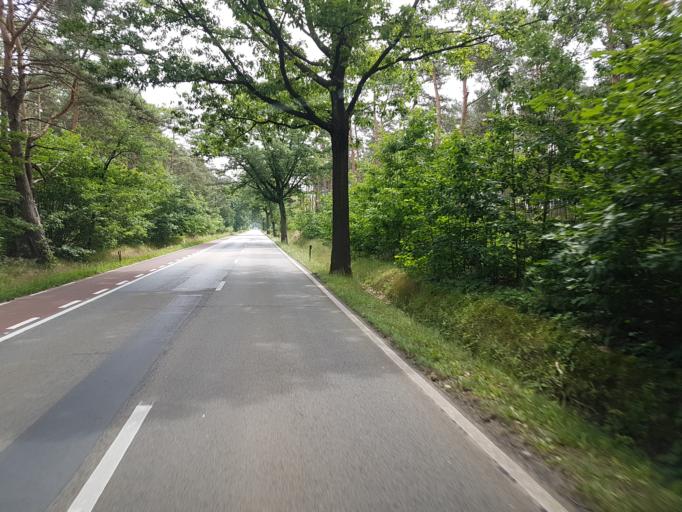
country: BE
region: Flanders
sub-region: Provincie Antwerpen
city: Oostmalle
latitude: 51.2777
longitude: 4.7662
